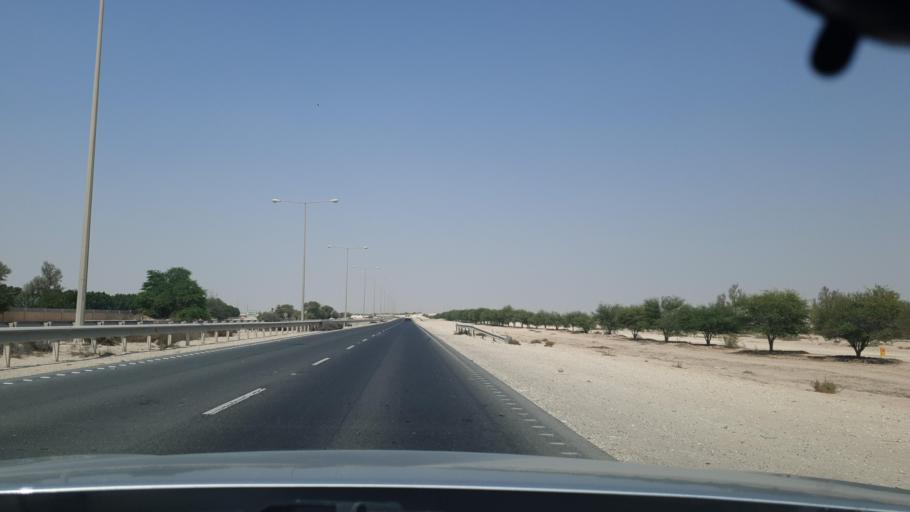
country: QA
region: Al Khawr
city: Al Khawr
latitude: 25.7285
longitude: 51.4957
